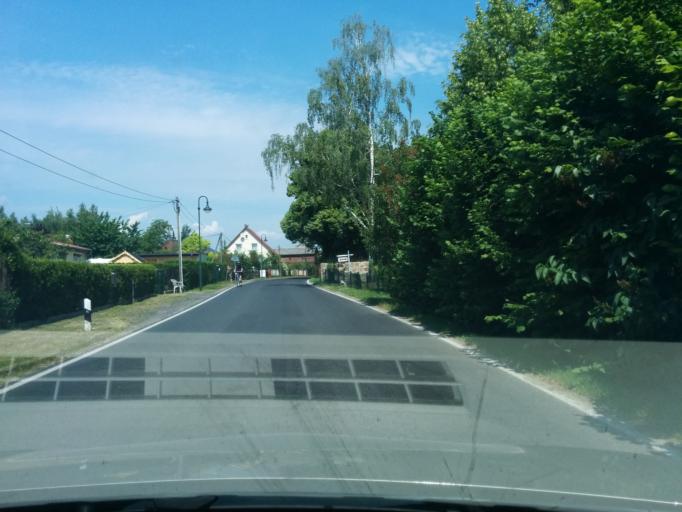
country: DE
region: Brandenburg
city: Ahrensfelde
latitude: 52.6269
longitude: 13.5745
